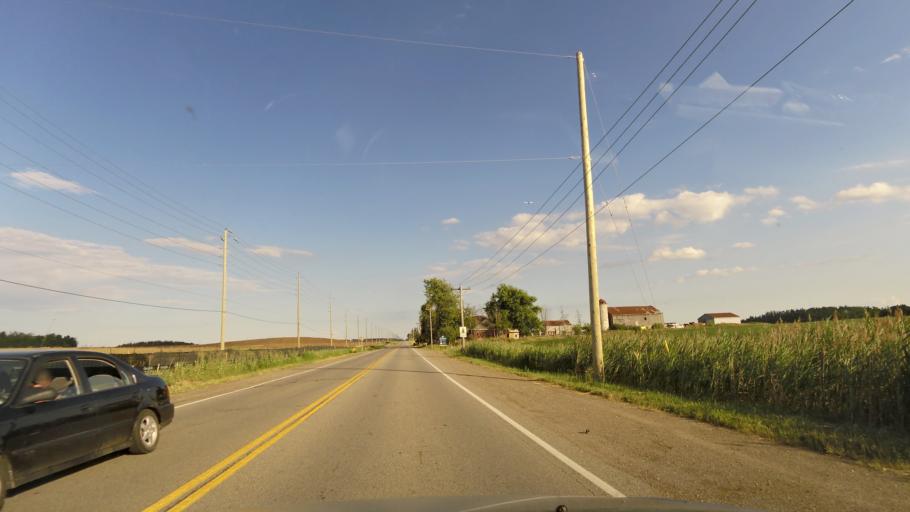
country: CA
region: Ontario
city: Brampton
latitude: 43.6939
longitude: -79.8663
